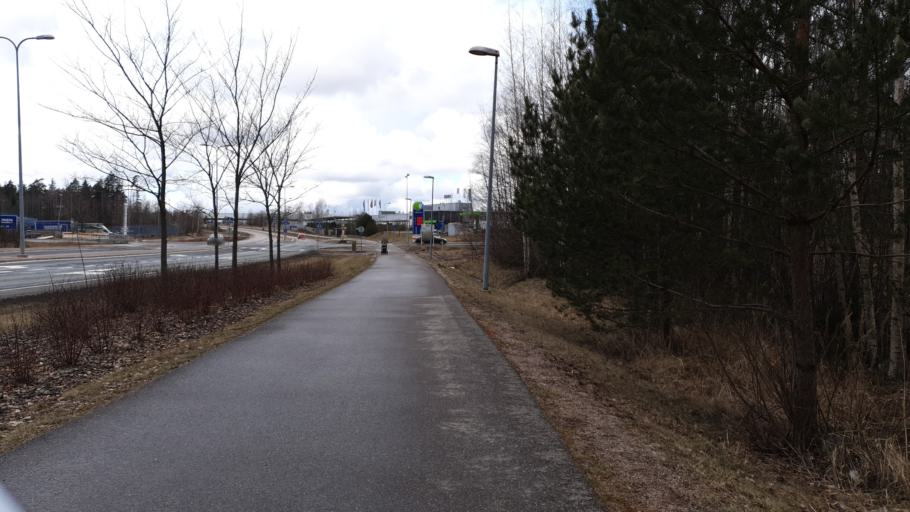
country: FI
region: Uusimaa
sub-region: Helsinki
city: Vantaa
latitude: 60.2944
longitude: 24.9251
